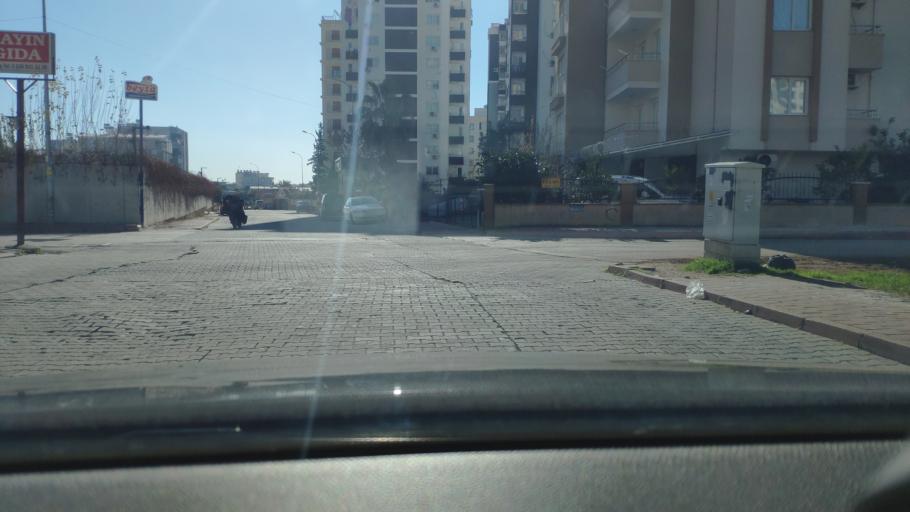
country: TR
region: Adana
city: Seyhan
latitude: 37.0228
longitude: 35.2683
